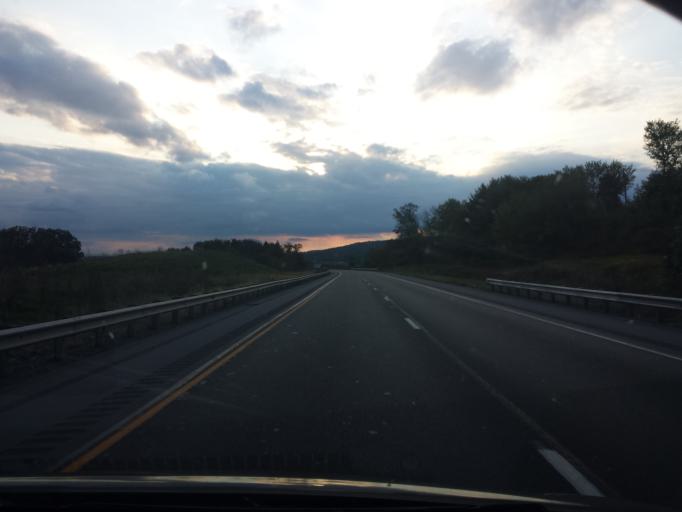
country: US
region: Pennsylvania
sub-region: Montour County
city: Danville
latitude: 41.0004
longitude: -76.6255
